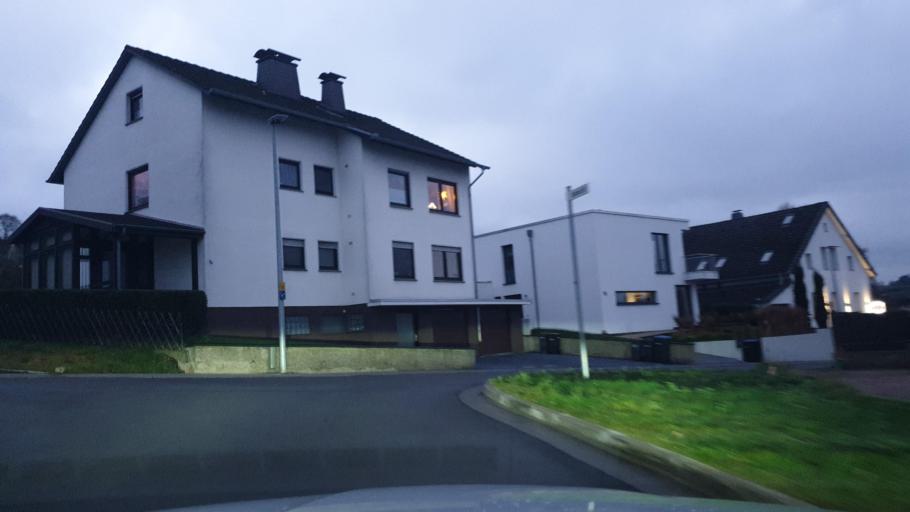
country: DE
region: North Rhine-Westphalia
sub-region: Regierungsbezirk Detmold
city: Vlotho
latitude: 52.1629
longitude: 8.8683
